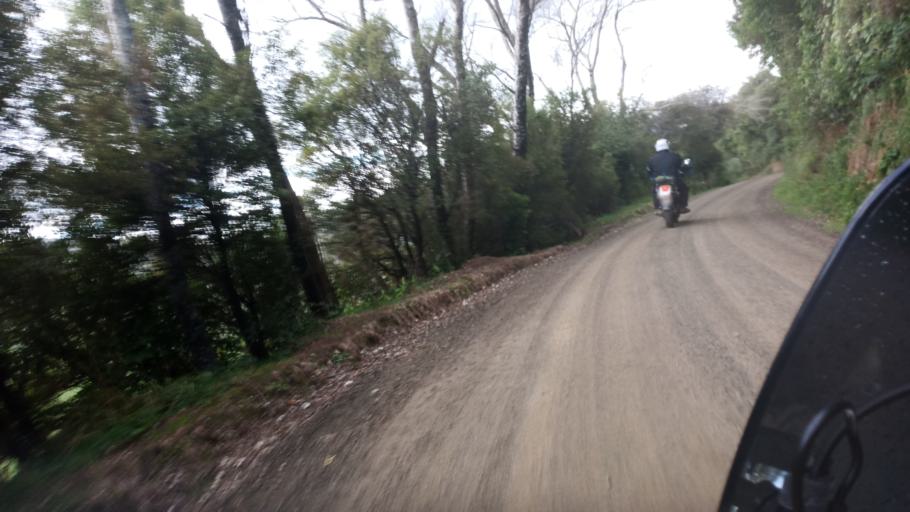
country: NZ
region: Gisborne
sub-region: Gisborne District
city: Gisborne
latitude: -38.4746
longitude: 177.6152
